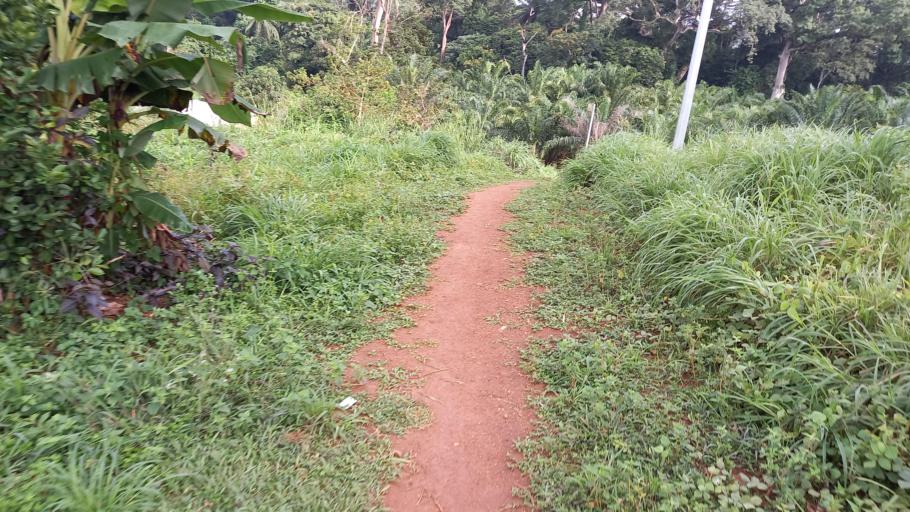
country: SL
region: Eastern Province
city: Kailahun
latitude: 8.2795
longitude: -10.5804
